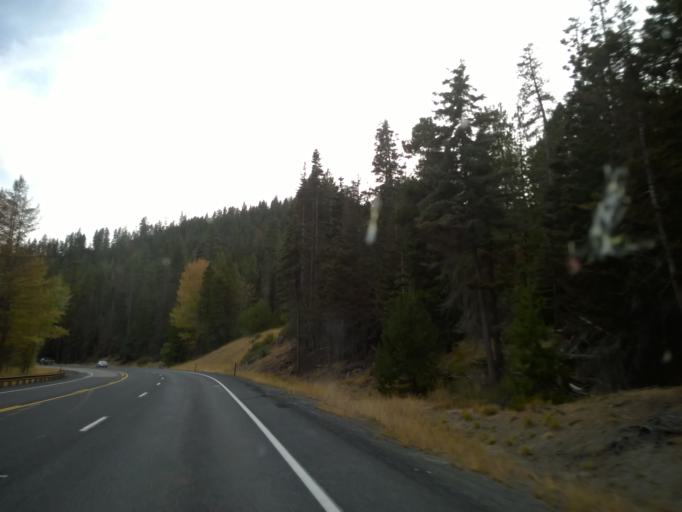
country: US
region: Washington
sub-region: Chelan County
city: Cashmere
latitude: 47.3521
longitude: -120.5702
